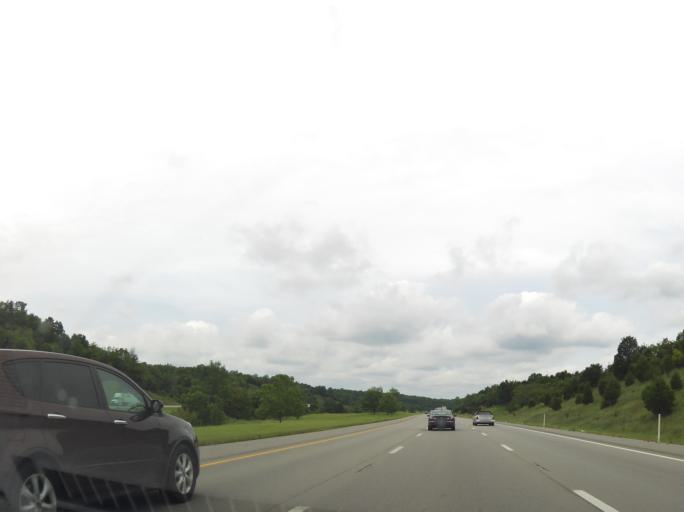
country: US
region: Kentucky
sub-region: Scott County
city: Georgetown
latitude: 38.3342
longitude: -84.5641
